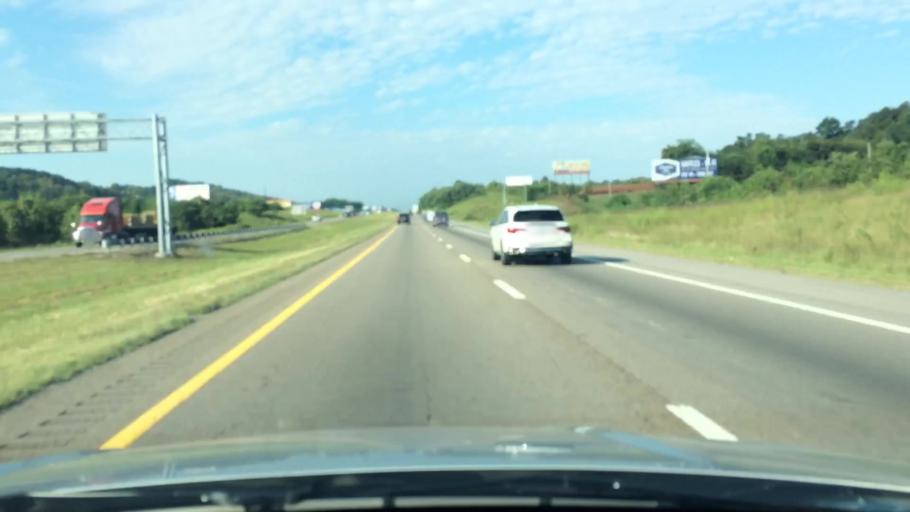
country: US
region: Tennessee
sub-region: Loudon County
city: Lenoir City
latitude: 35.8184
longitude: -84.2936
